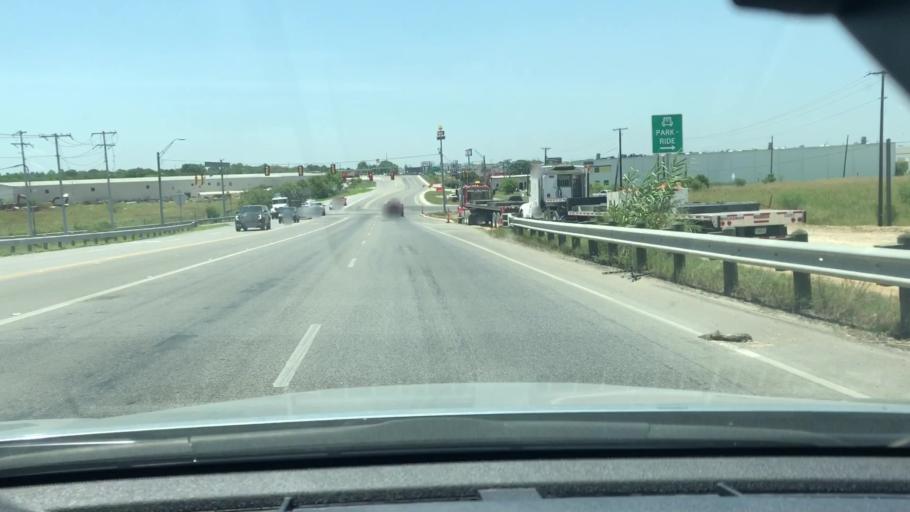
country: US
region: Texas
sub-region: Comal County
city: New Braunfels
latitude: 29.6801
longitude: -98.1550
